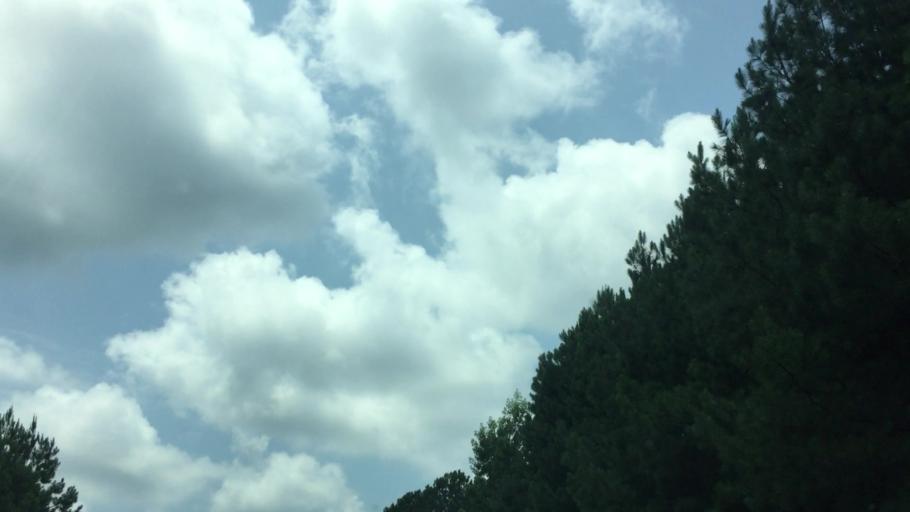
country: US
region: Georgia
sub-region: Fulton County
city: Chattahoochee Hills
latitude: 33.5699
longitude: -84.7299
